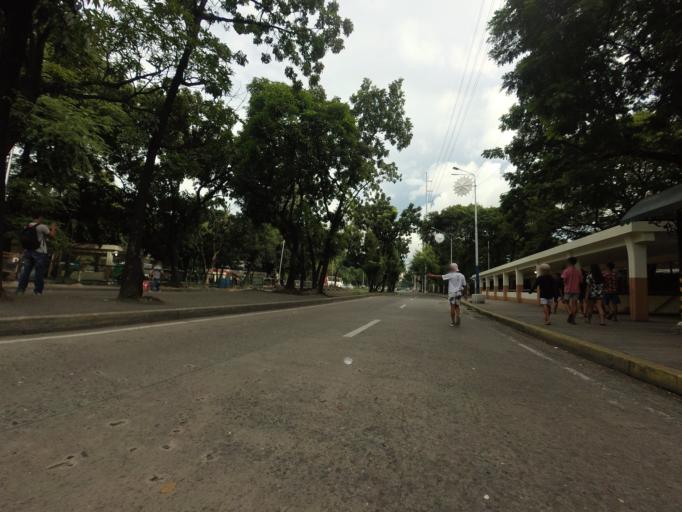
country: PH
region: Metro Manila
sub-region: City of Manila
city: Quiapo
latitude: 14.5937
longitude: 120.9785
